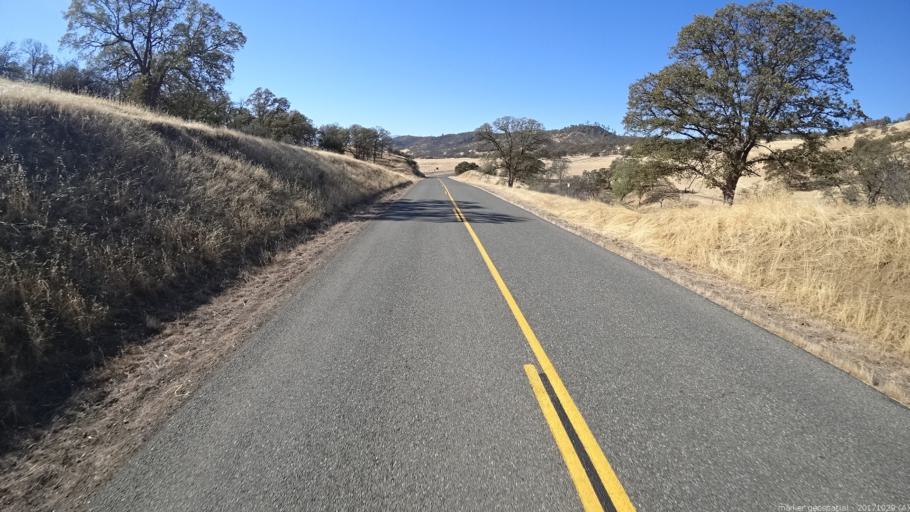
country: US
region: California
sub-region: Shasta County
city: Shasta
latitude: 40.4405
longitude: -122.6591
